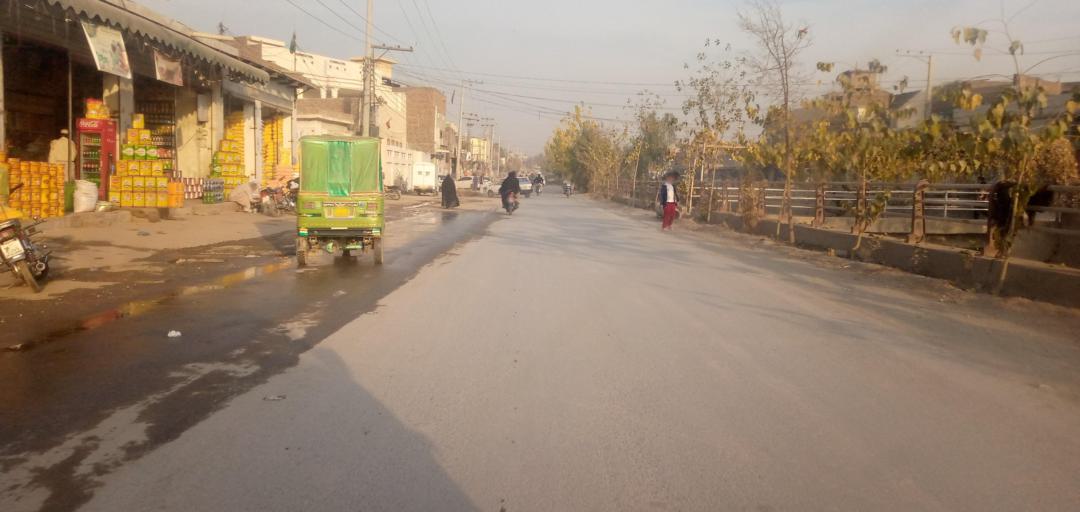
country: PK
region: Khyber Pakhtunkhwa
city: Peshawar
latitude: 33.9730
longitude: 71.5229
